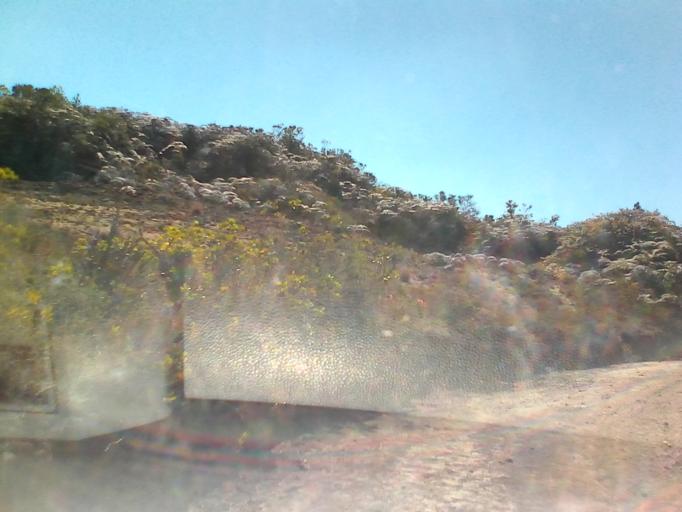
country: CO
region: Boyaca
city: Sachica
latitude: 5.5339
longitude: -73.5492
